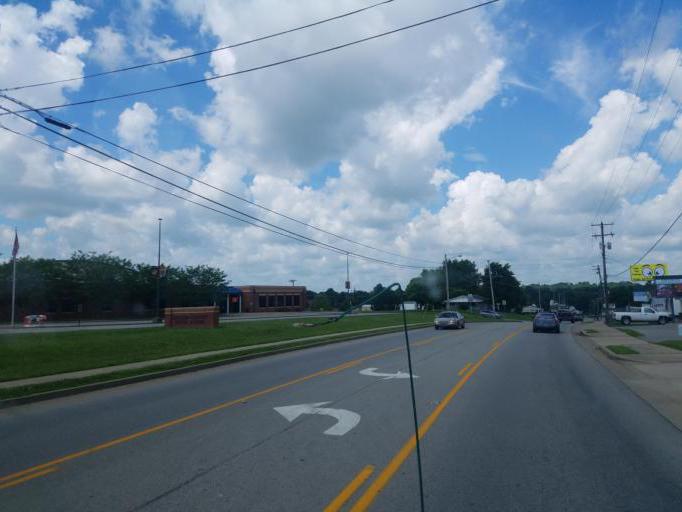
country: US
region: Kentucky
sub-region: Grayson County
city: Leitchfield
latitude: 37.4837
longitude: -86.2822
